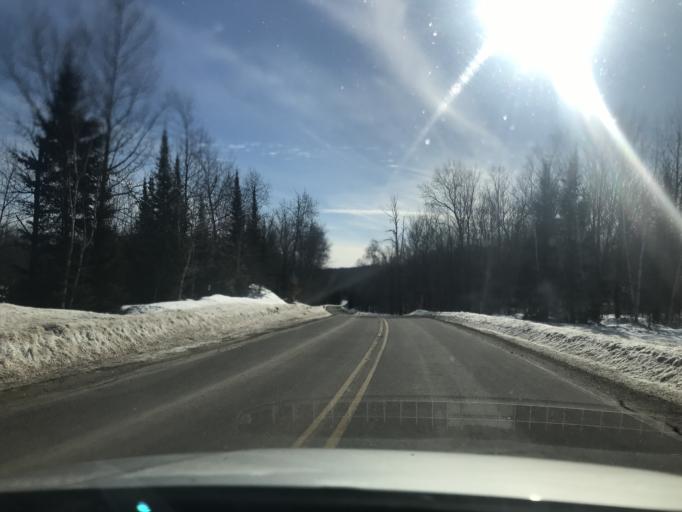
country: US
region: Michigan
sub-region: Dickinson County
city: Kingsford
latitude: 45.4148
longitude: -88.3941
